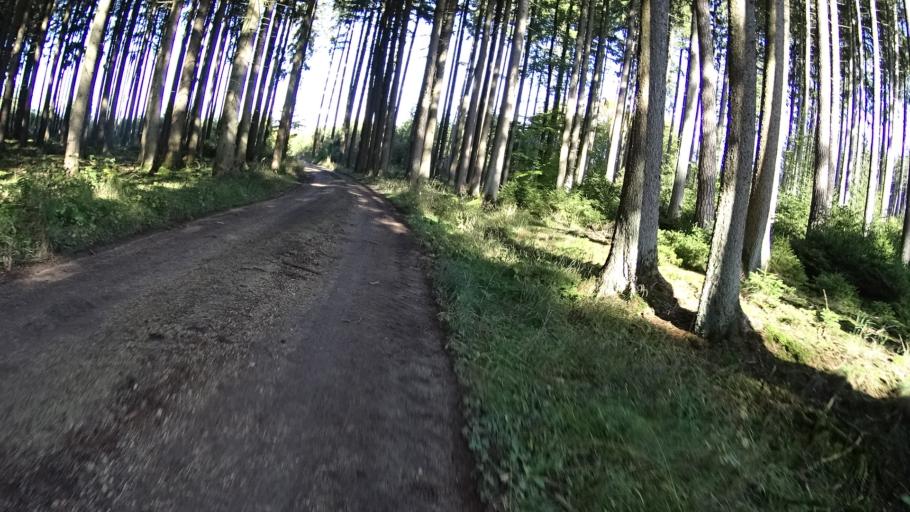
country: DE
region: Bavaria
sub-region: Upper Bavaria
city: Bohmfeld
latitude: 48.8783
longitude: 11.3679
